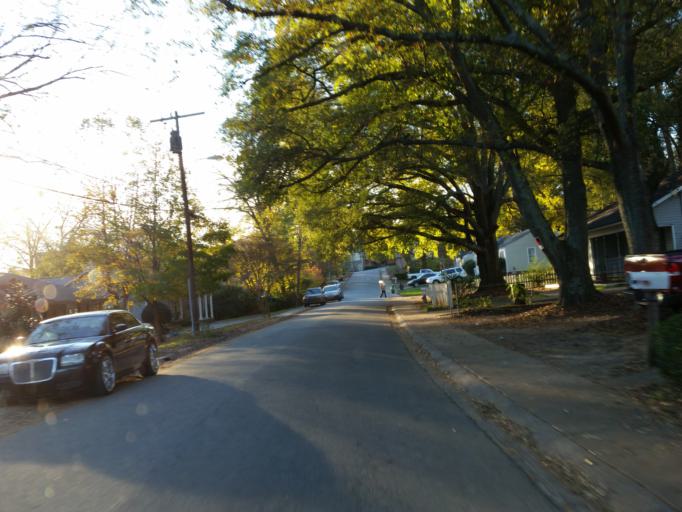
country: US
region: Georgia
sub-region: Cobb County
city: Marietta
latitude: 33.9567
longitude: -84.5413
